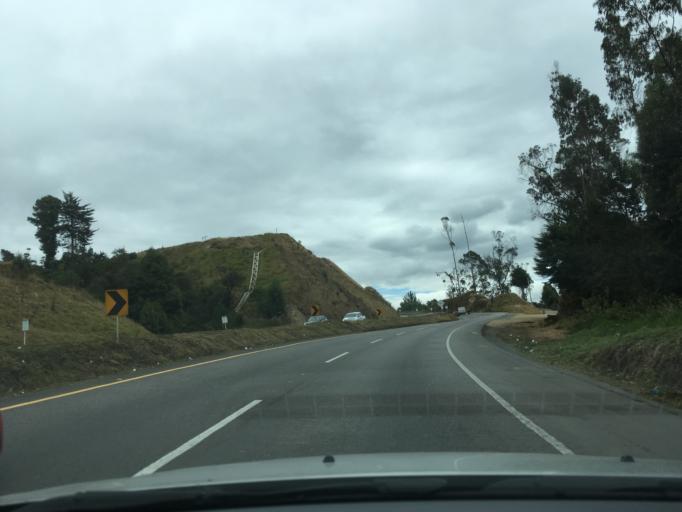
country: CO
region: Boyaca
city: Samaca
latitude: 5.4549
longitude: -73.4226
